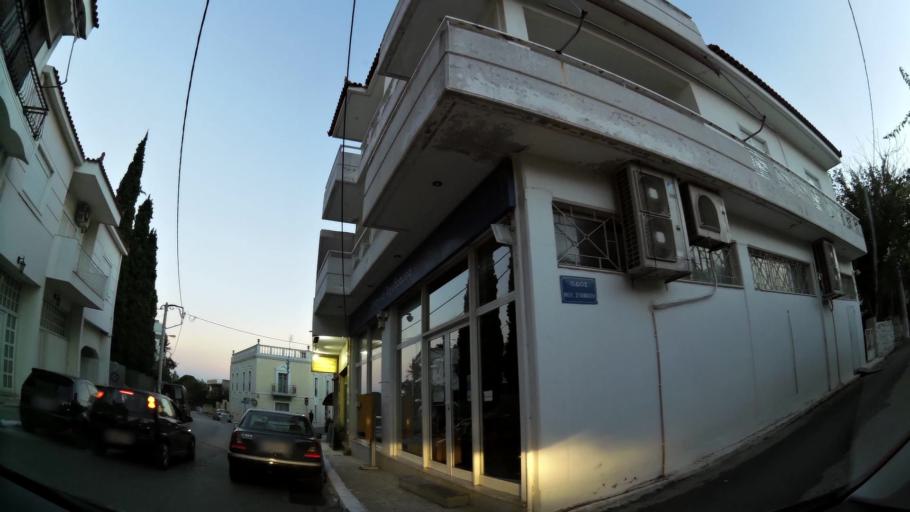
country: GR
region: Attica
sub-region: Nomarchia Anatolikis Attikis
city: Paiania
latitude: 37.9522
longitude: 23.8528
